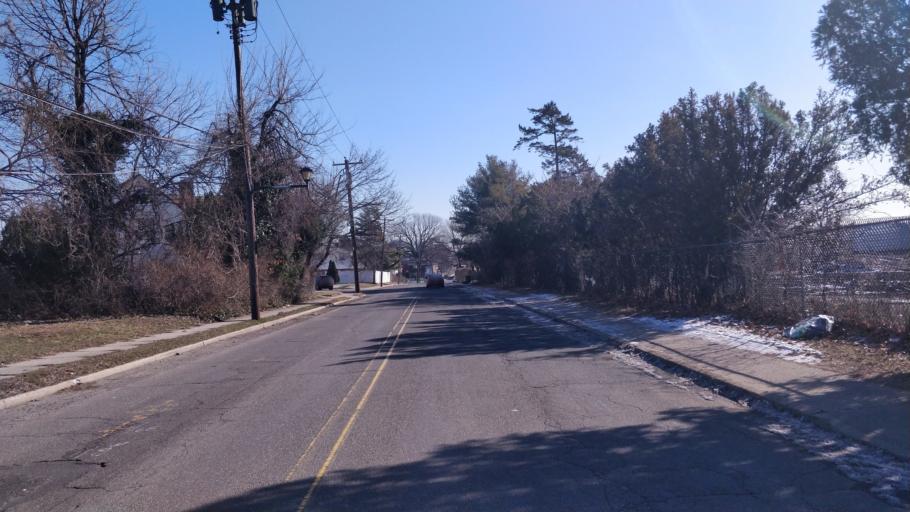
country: US
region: New York
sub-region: Nassau County
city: Westbury
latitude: 40.7600
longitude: -73.5807
